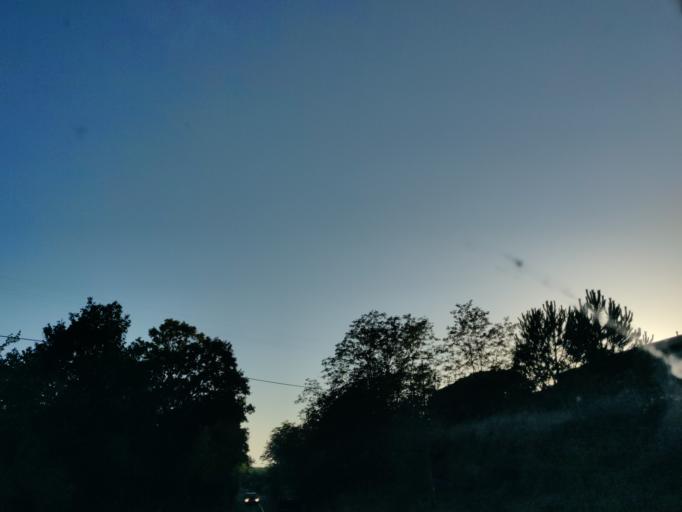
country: IT
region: Latium
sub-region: Provincia di Viterbo
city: Canino
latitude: 42.4324
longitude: 11.7193
